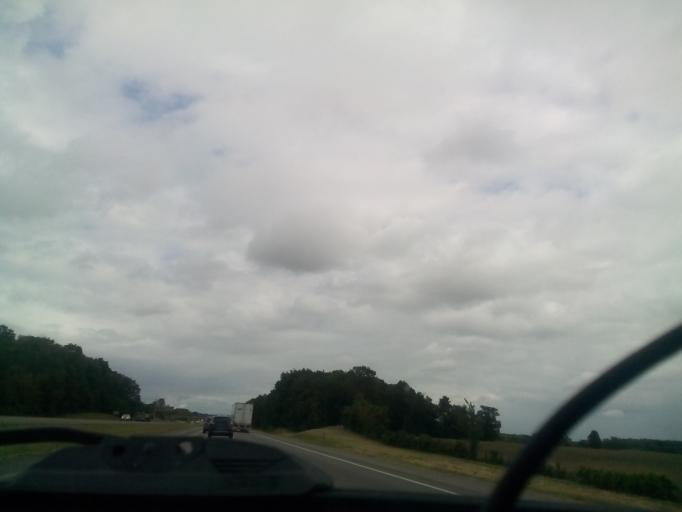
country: US
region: Ohio
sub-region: Williams County
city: Montpelier
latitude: 41.6283
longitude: -84.7376
